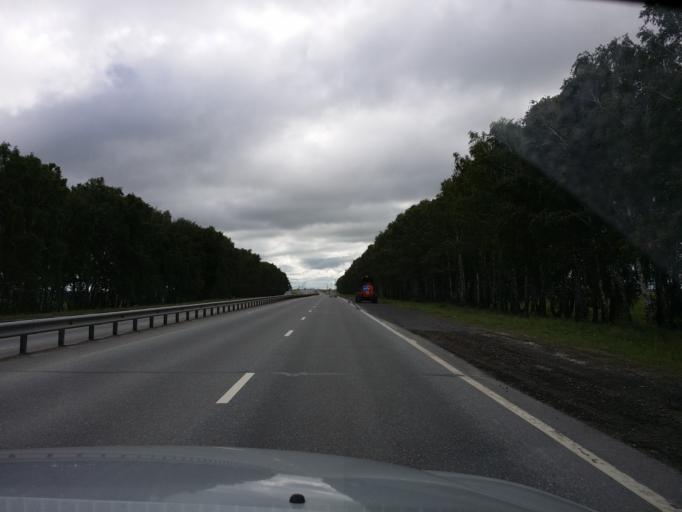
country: RU
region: Tjumen
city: Antipino
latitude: 57.1594
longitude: 65.8317
